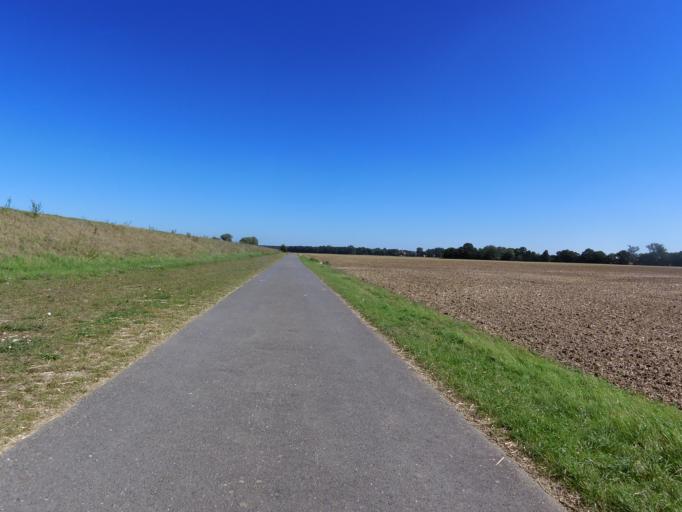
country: DE
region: Saxony-Anhalt
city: Pretzsch
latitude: 51.7372
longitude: 12.8187
